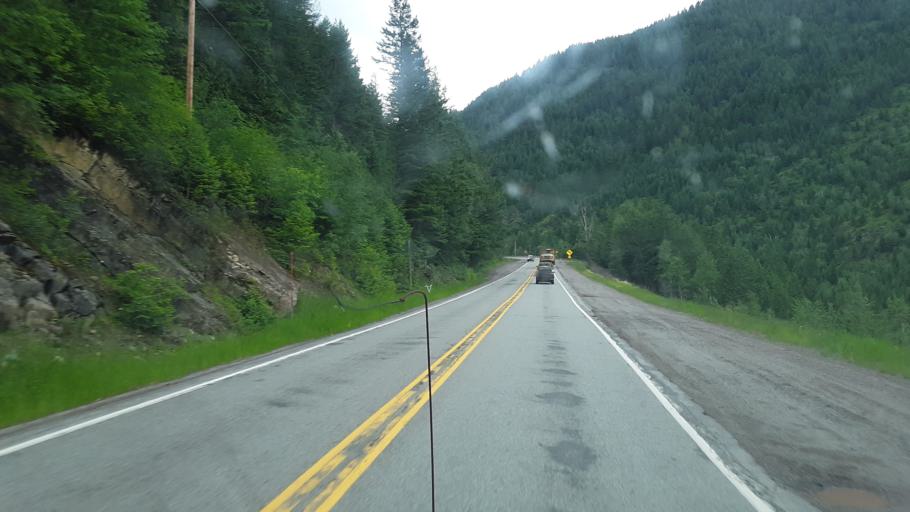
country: US
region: Montana
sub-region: Flathead County
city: Columbia Falls
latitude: 48.4988
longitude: -113.9280
